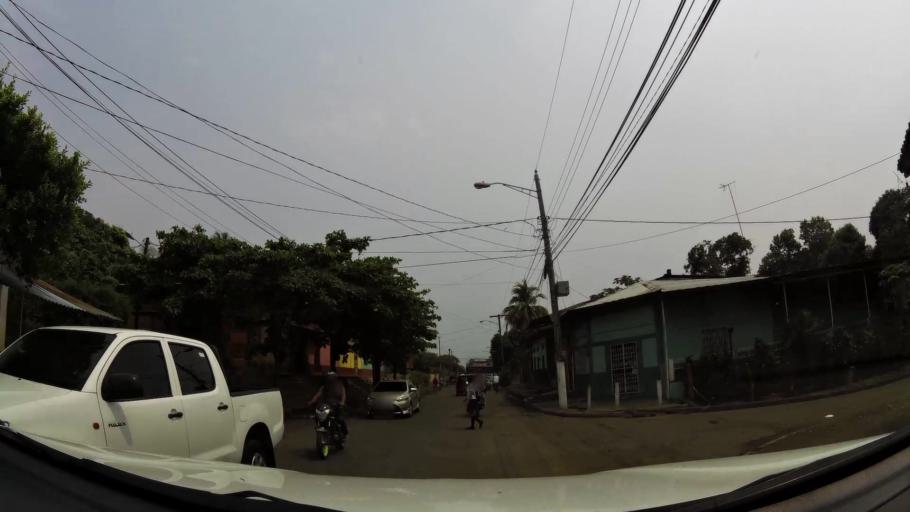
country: NI
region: Chinandega
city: Chinandega
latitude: 12.6375
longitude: -87.1319
